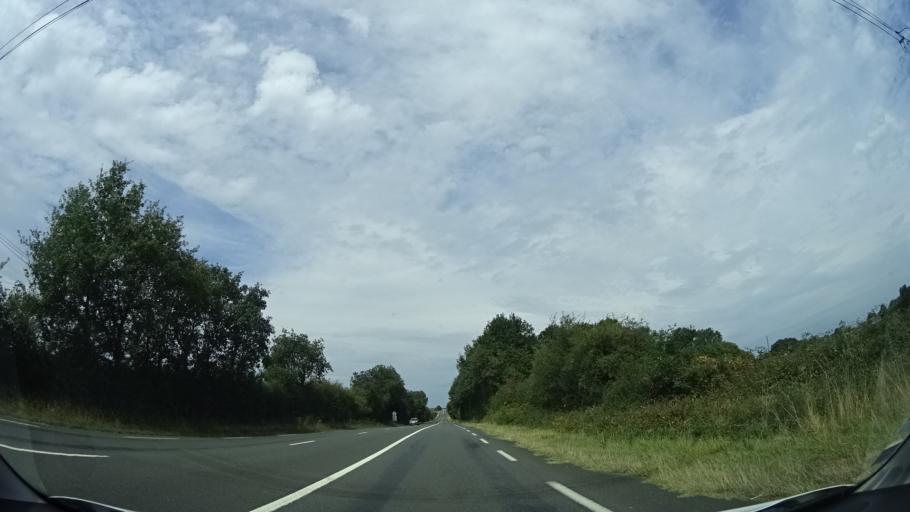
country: FR
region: Pays de la Loire
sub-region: Departement de la Sarthe
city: Vion
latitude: 47.7691
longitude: -0.1999
